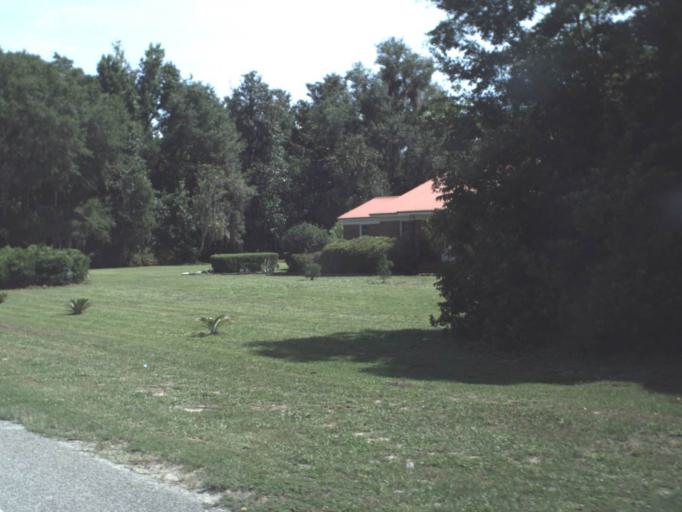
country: US
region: Florida
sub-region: Hamilton County
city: Jasper
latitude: 30.4318
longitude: -82.9337
